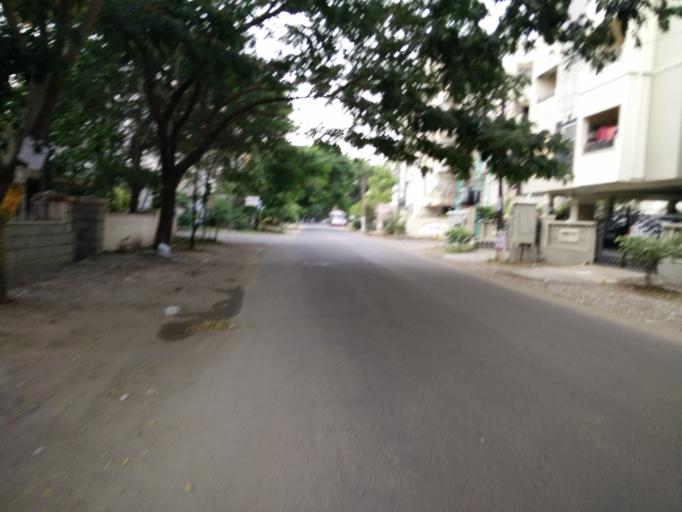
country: IN
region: Tamil Nadu
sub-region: Coimbatore
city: Coimbatore
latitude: 11.0248
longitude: 76.9418
